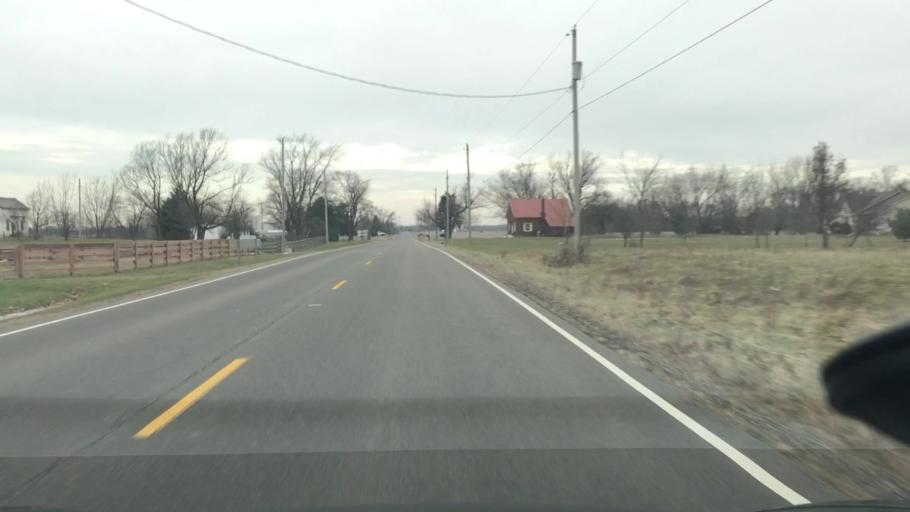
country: US
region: Ohio
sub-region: Madison County
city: London
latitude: 39.8348
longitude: -83.3754
